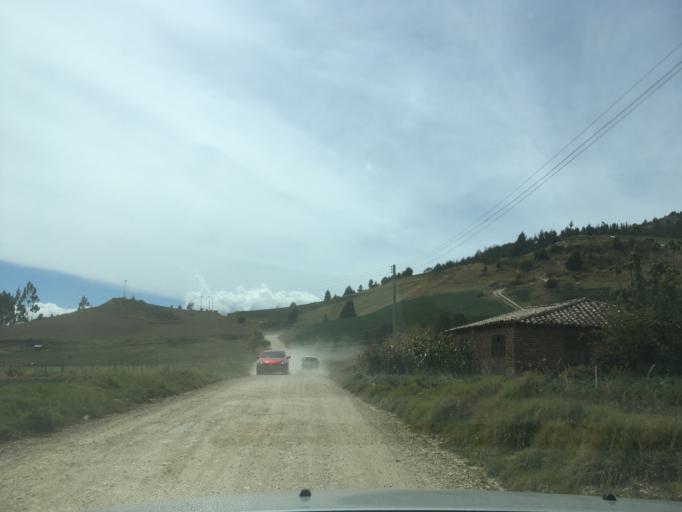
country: CO
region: Boyaca
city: Aquitania
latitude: 5.5971
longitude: -72.9170
